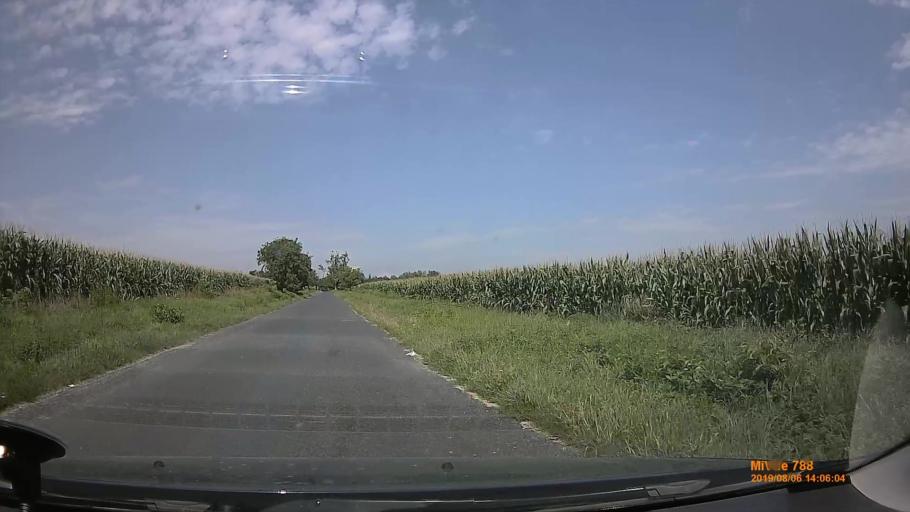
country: HU
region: Zala
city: Zalakomar
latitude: 46.5179
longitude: 17.0850
